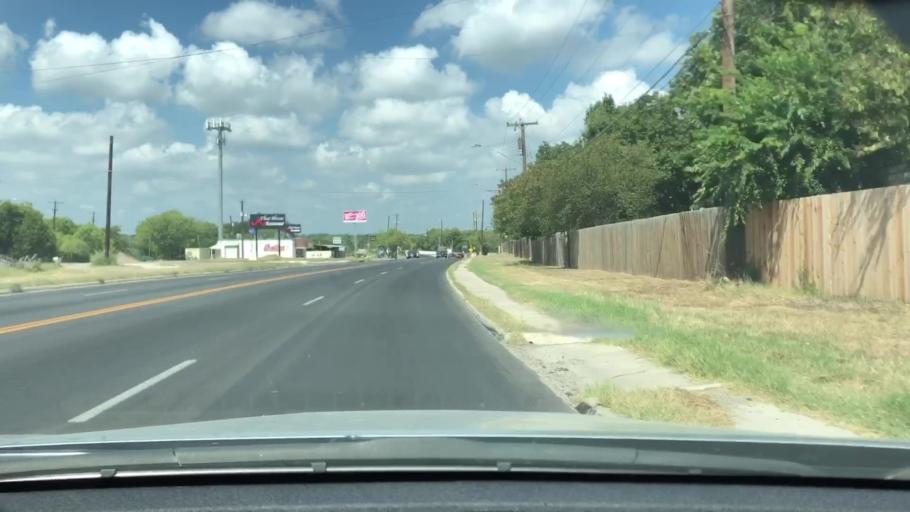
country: US
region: Texas
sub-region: Bexar County
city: Kirby
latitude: 29.4842
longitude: -98.4117
